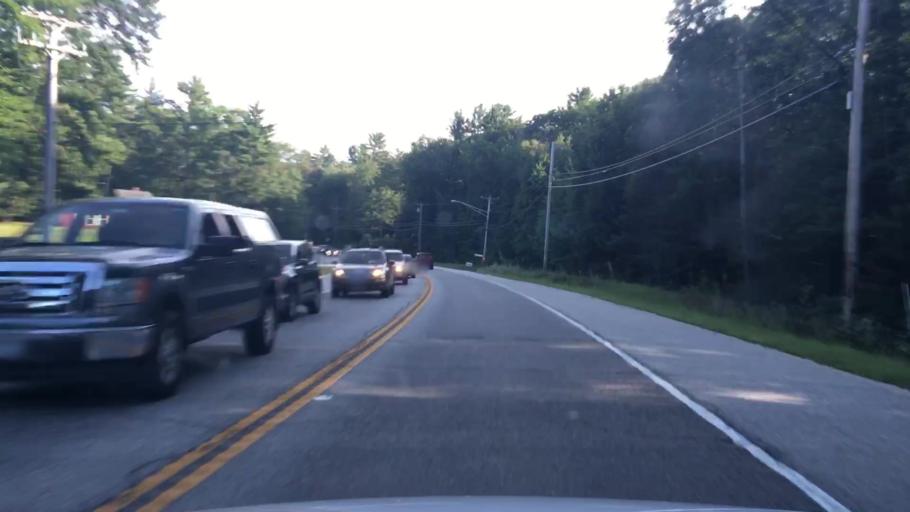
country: US
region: Maine
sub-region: Cumberland County
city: Raymond
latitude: 43.8643
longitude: -70.4663
